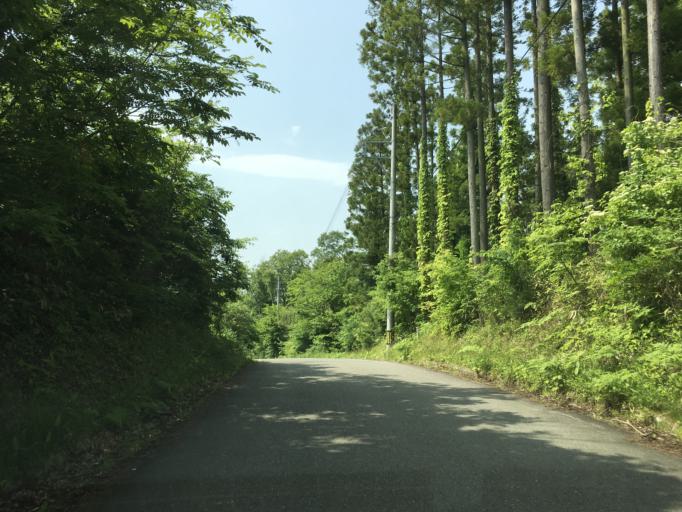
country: JP
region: Iwate
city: Hanamaki
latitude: 39.3954
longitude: 141.1736
